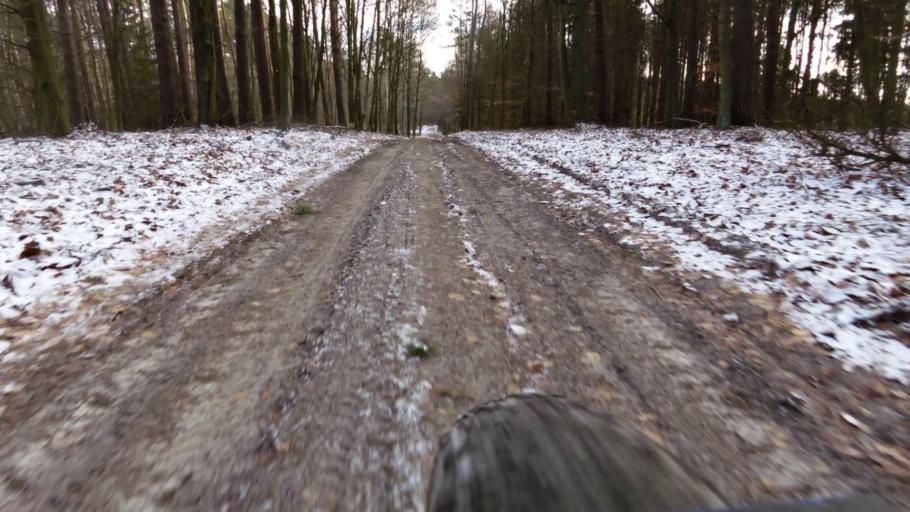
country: PL
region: West Pomeranian Voivodeship
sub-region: Powiat walecki
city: Walcz
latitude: 53.2794
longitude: 16.3061
